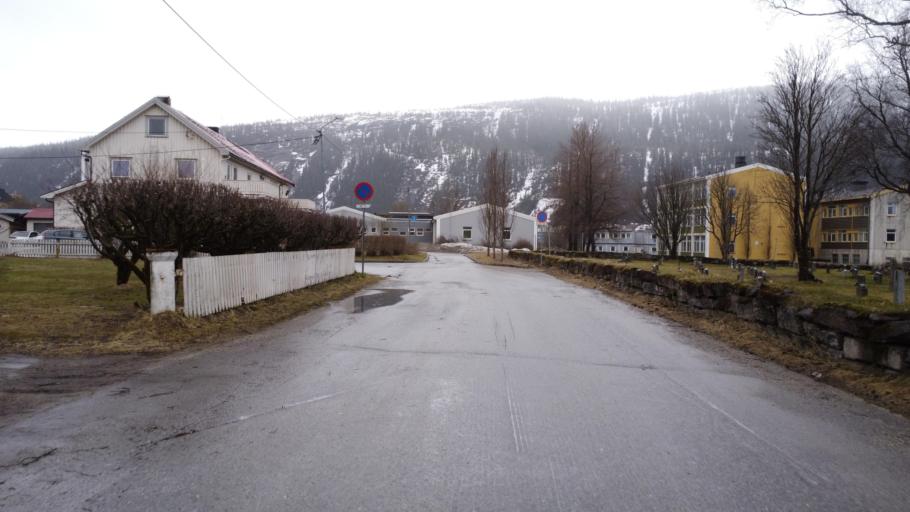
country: NO
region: Nordland
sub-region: Rana
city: Mo i Rana
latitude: 66.3101
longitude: 14.1469
